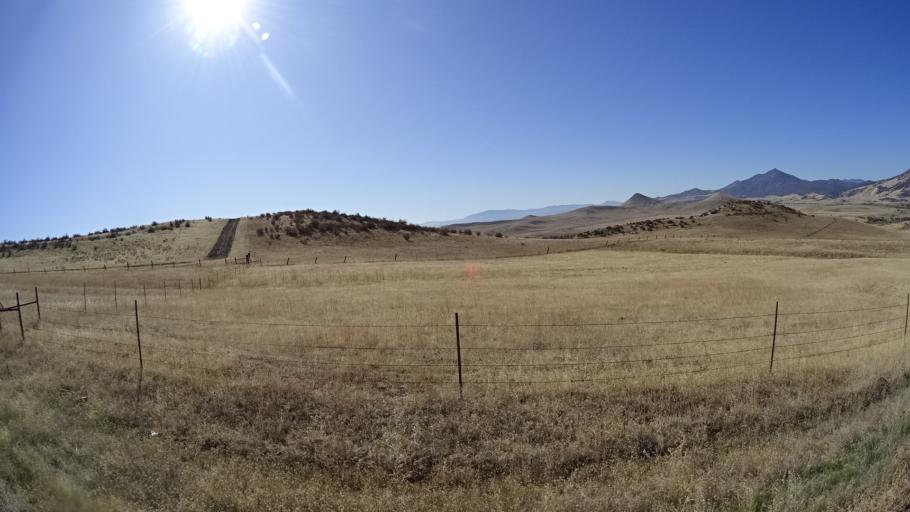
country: US
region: California
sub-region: Siskiyou County
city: Montague
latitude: 41.8450
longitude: -122.4304
